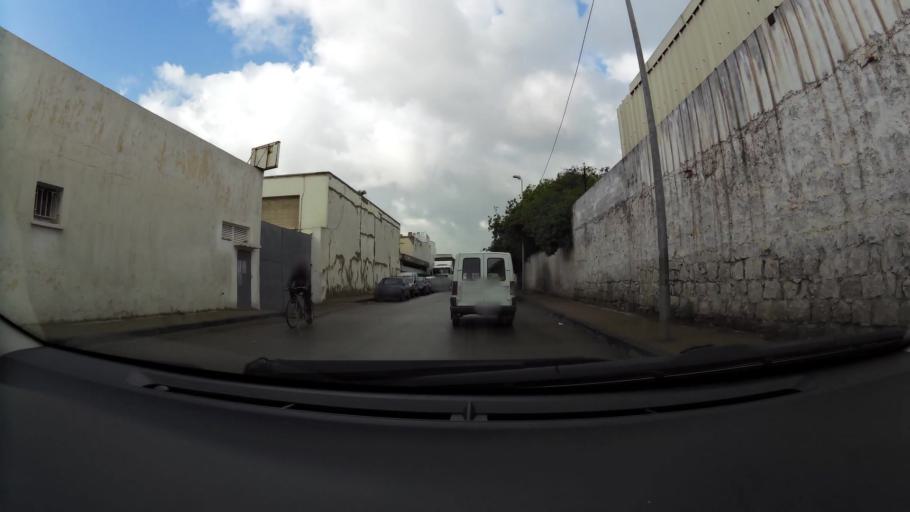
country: MA
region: Grand Casablanca
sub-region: Mediouna
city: Tit Mellil
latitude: 33.5919
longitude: -7.5402
